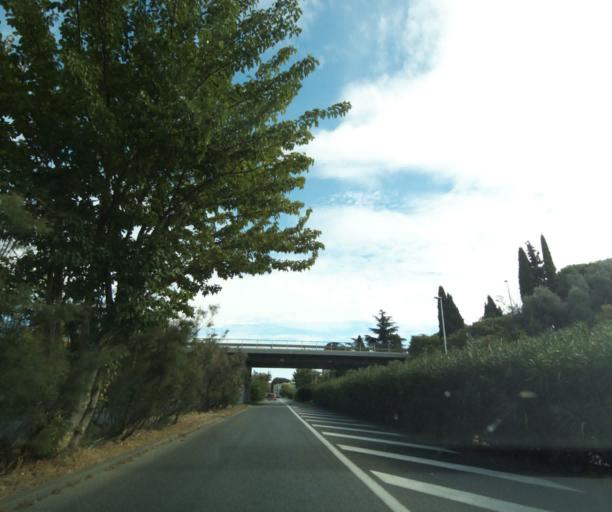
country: FR
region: Languedoc-Roussillon
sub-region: Departement de l'Herault
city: Juvignac
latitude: 43.6095
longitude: 3.8379
